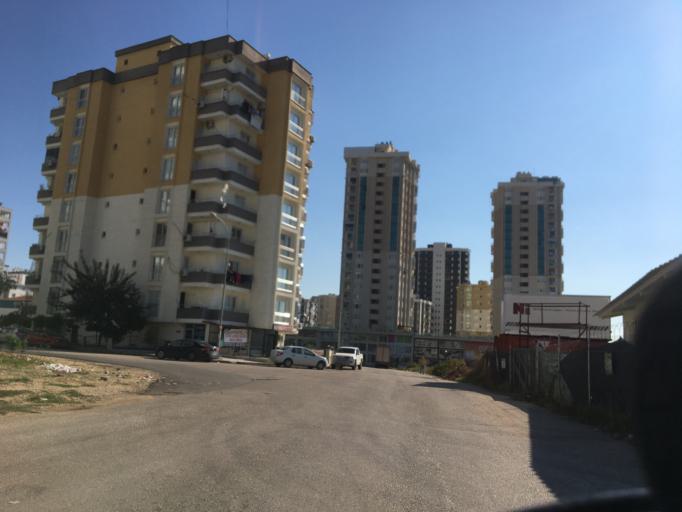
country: TR
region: Adana
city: Seyhan
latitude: 37.0188
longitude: 35.2853
